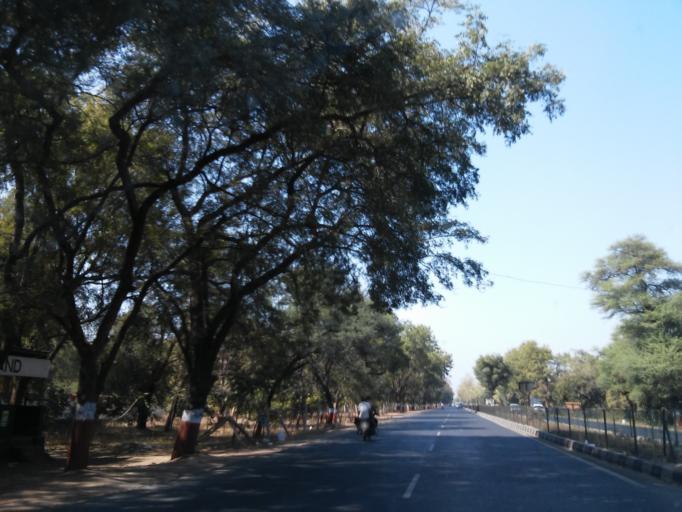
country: IN
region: Gujarat
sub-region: Gandhinagar
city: Ghandinagar
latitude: 23.2393
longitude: 72.7096
